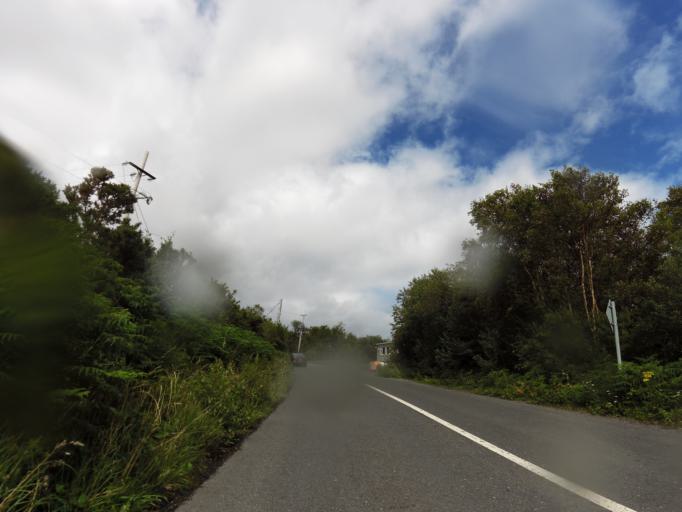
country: IE
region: Connaught
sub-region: County Galway
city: Oughterard
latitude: 53.4161
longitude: -9.3307
